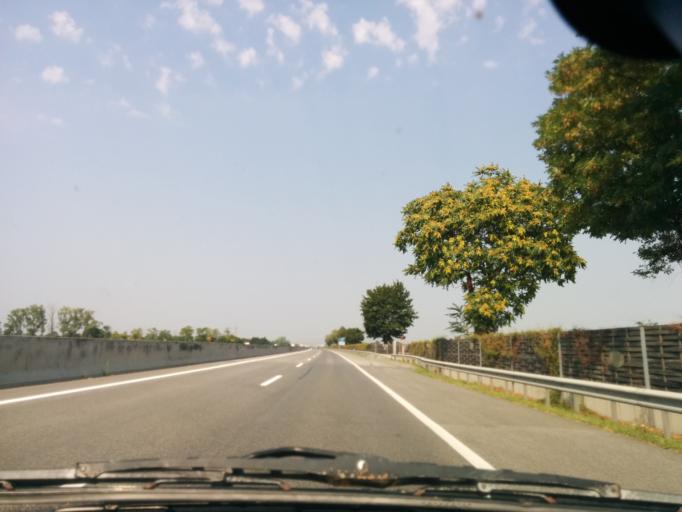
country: AT
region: Lower Austria
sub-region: Politischer Bezirk Tulln
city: Kirchberg am Wagram
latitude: 48.4039
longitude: 15.8945
